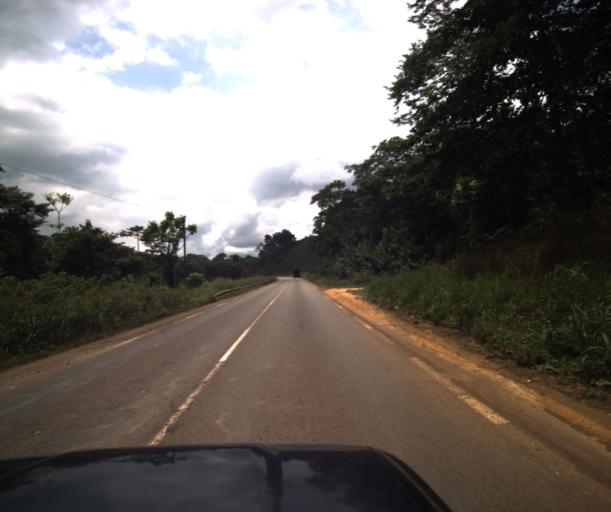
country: CM
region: Centre
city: Eseka
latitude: 3.8861
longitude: 10.7070
